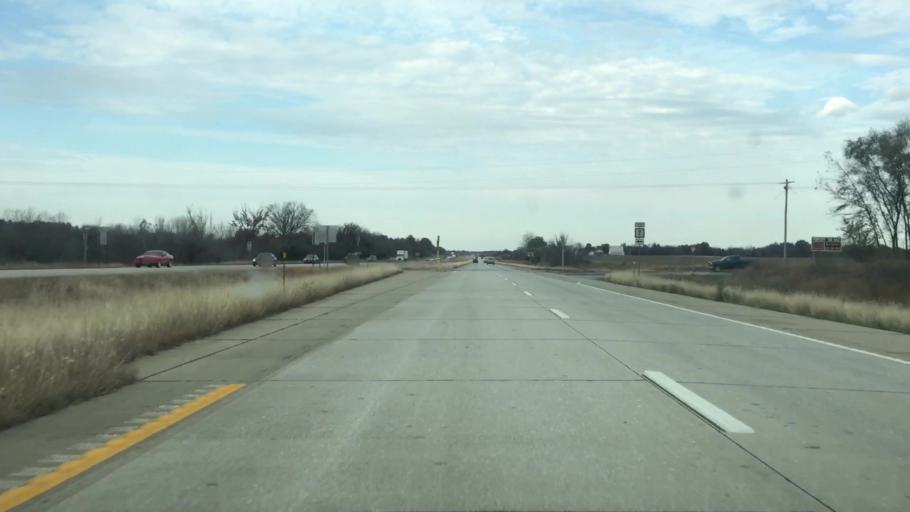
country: US
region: Missouri
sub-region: Henry County
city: Clinton
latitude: 38.3002
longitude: -93.7586
